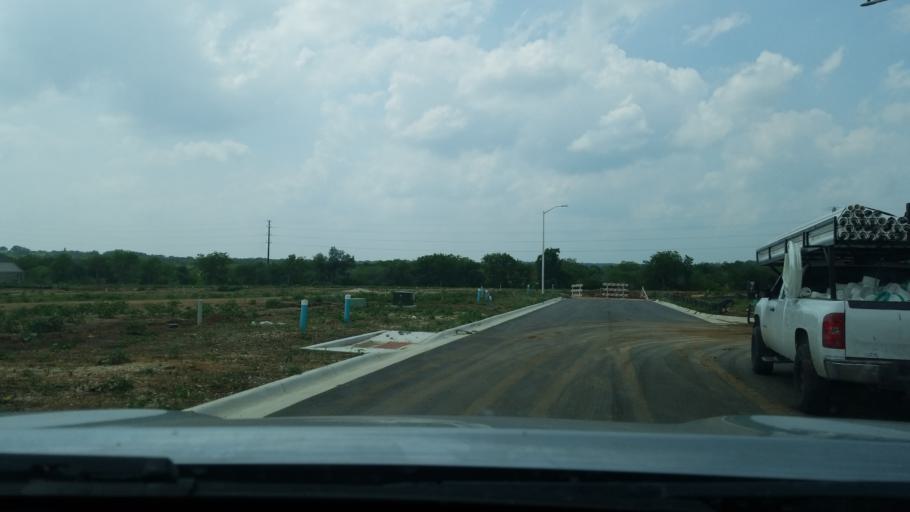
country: US
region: Texas
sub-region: Comal County
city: New Braunfels
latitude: 29.7488
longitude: -98.0943
